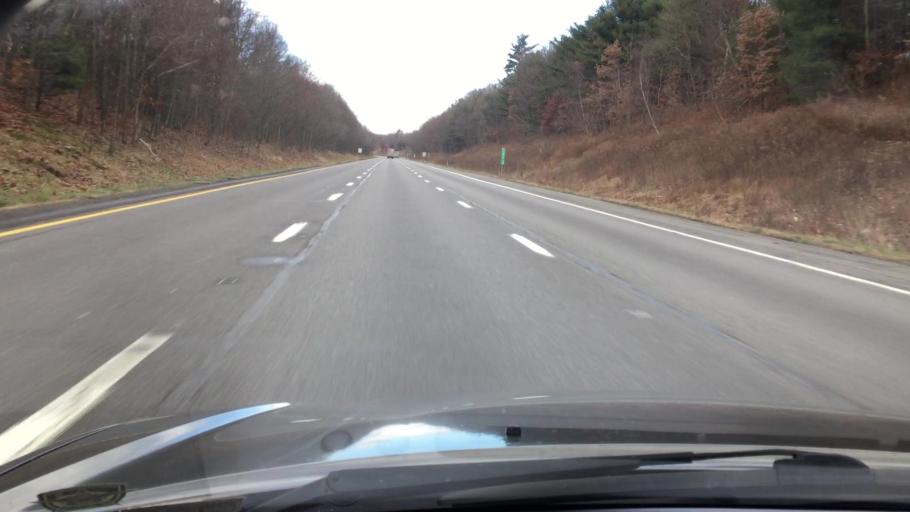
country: US
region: Pennsylvania
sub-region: Monroe County
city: Tannersville
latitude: 41.0576
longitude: -75.3226
